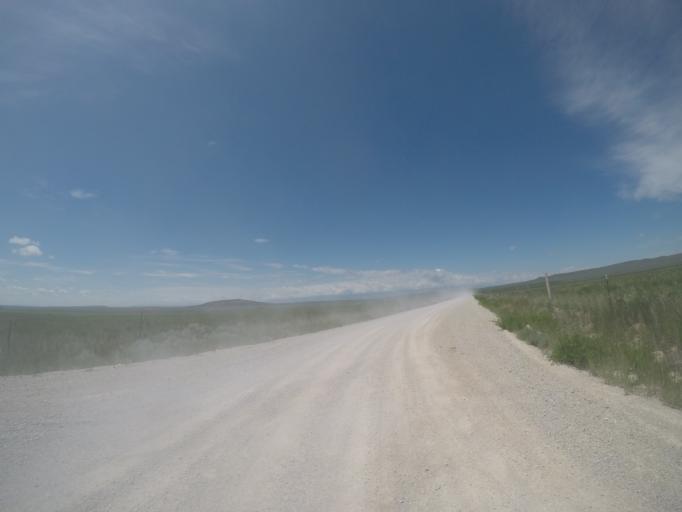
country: US
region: Montana
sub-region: Yellowstone County
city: Laurel
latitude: 45.2196
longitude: -108.6998
